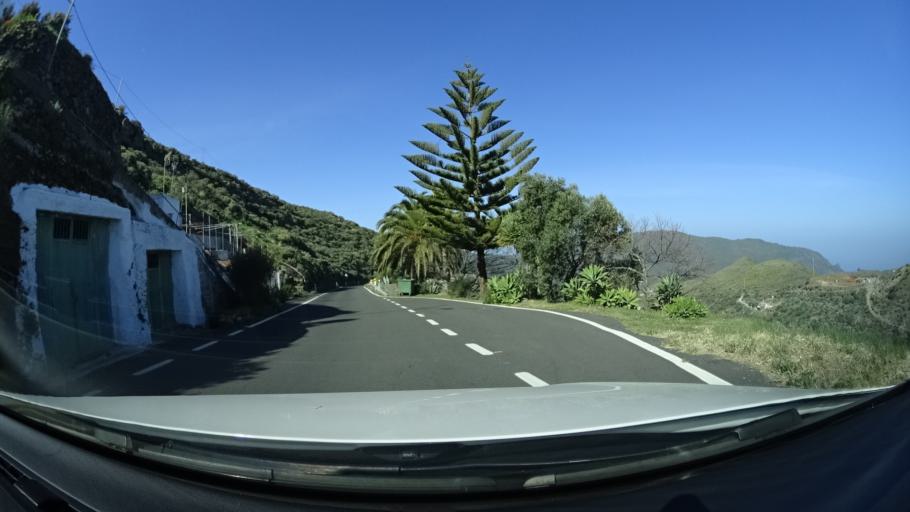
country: ES
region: Canary Islands
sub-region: Provincia de Las Palmas
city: Artenara
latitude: 28.0256
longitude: -15.6404
